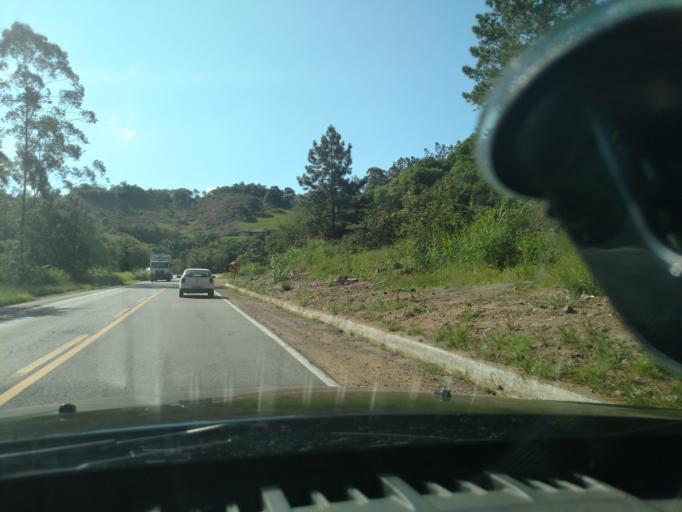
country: BR
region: Santa Catarina
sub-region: Ibirama
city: Ibirama
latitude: -27.0810
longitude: -49.5132
